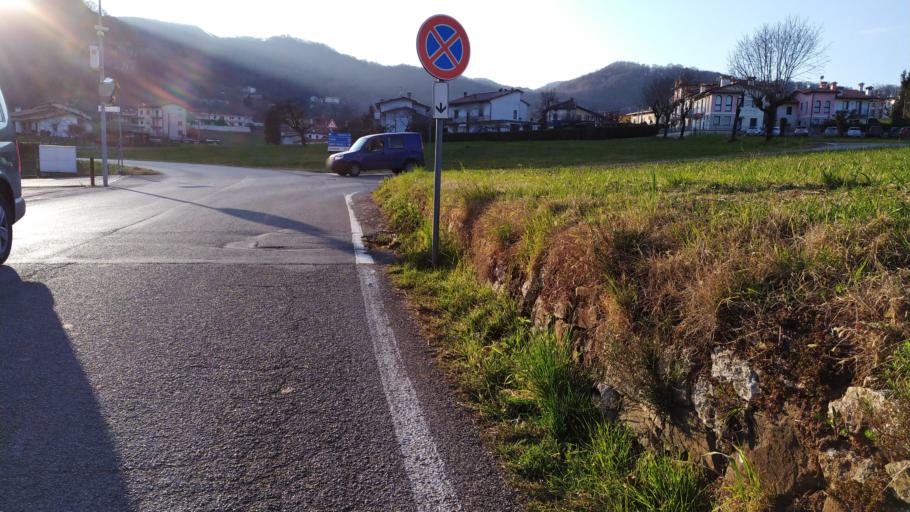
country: IT
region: Veneto
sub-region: Provincia di Vicenza
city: Monte di Malo
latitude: 45.6612
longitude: 11.3582
